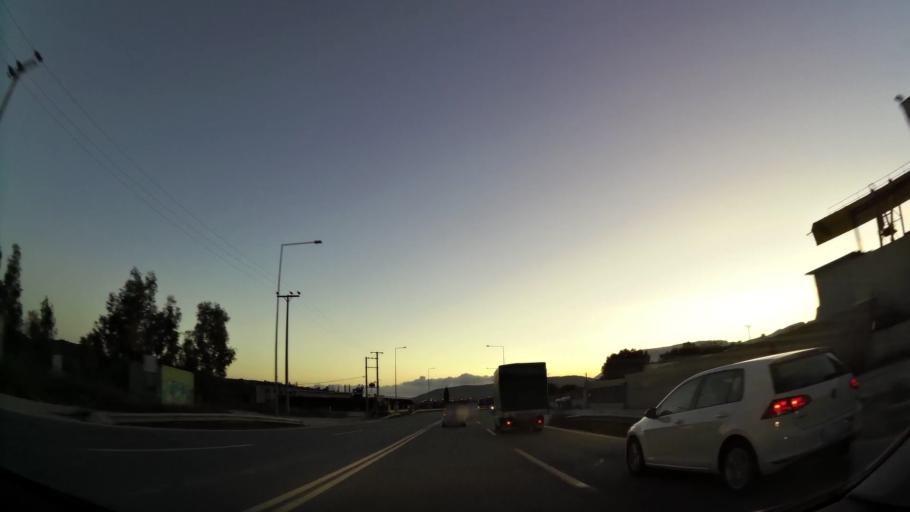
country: GR
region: Attica
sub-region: Nomarchia Anatolikis Attikis
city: Pikermi
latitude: 37.9963
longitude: 23.9229
